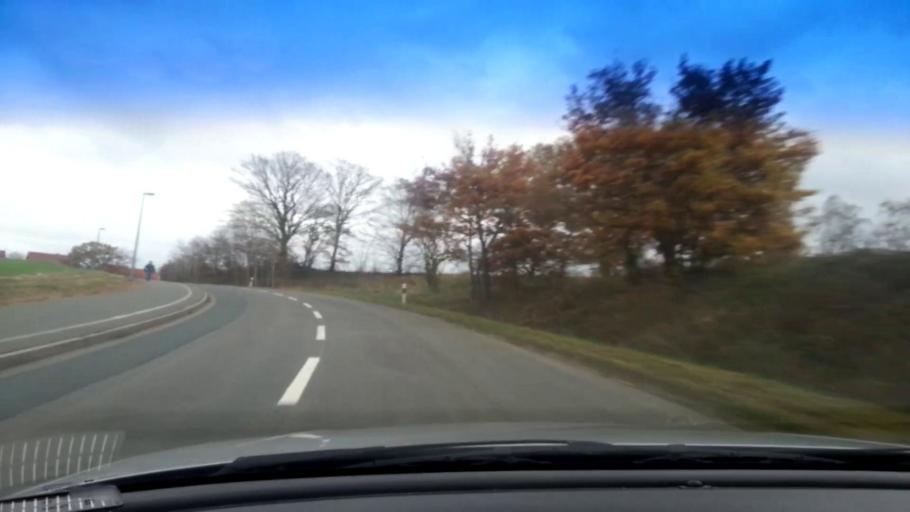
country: DE
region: Bavaria
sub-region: Upper Franconia
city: Stegaurach
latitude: 49.8715
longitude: 10.8672
